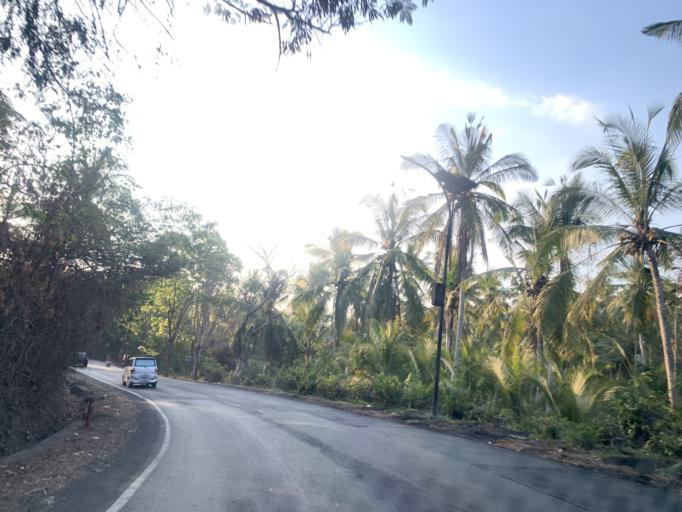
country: ID
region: Bali
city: Angkahgede
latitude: -8.4846
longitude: 114.9492
